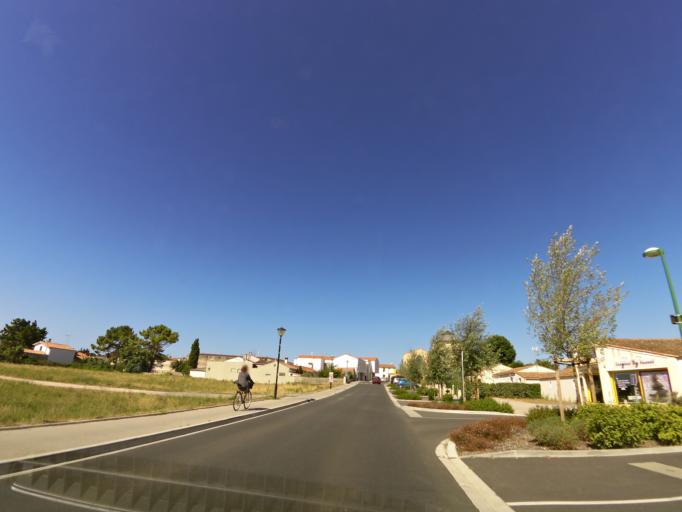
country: FR
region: Pays de la Loire
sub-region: Departement de la Vendee
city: Jard-sur-Mer
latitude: 46.4156
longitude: -1.5463
